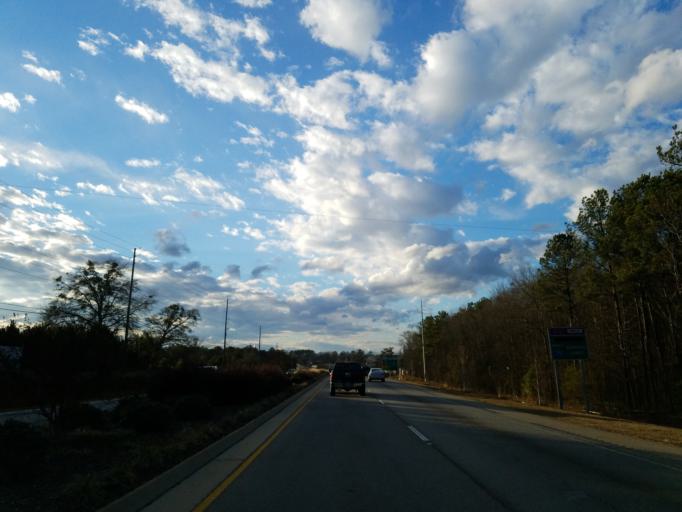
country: US
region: Georgia
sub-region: Henry County
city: McDonough
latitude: 33.4606
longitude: -84.1989
